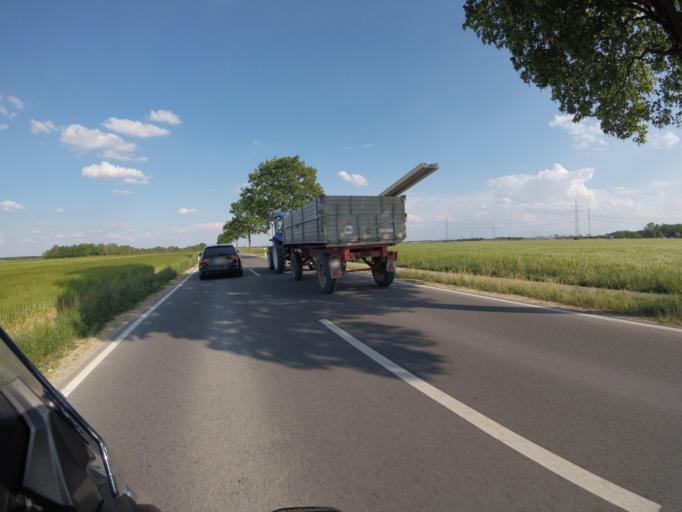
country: DE
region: Bavaria
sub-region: Upper Bavaria
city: Eching
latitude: 48.2925
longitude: 11.6385
